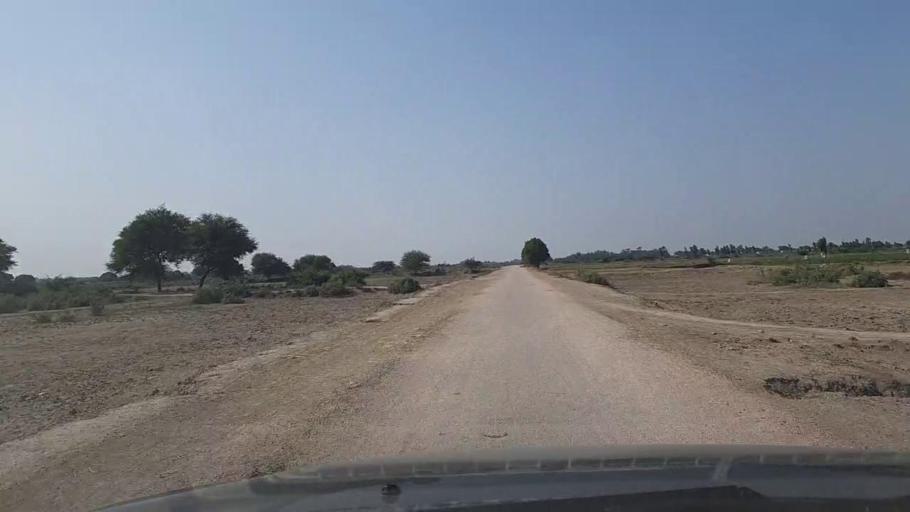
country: PK
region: Sindh
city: Mirpur Sakro
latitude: 24.4061
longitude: 67.6859
